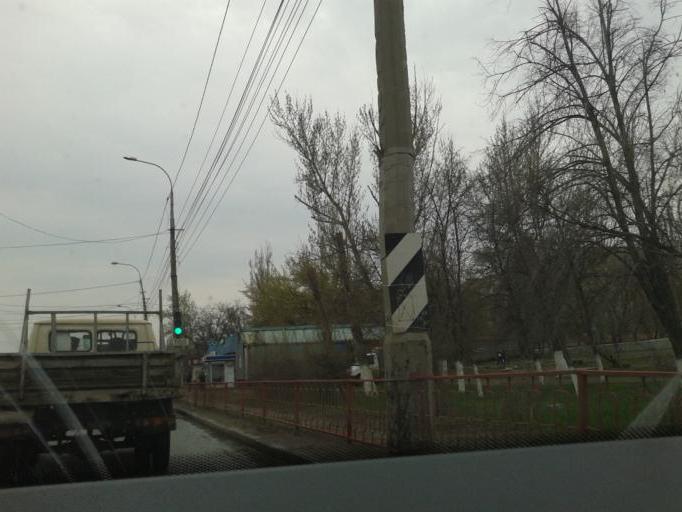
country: RU
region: Volgograd
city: Volgograd
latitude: 48.6495
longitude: 44.4346
